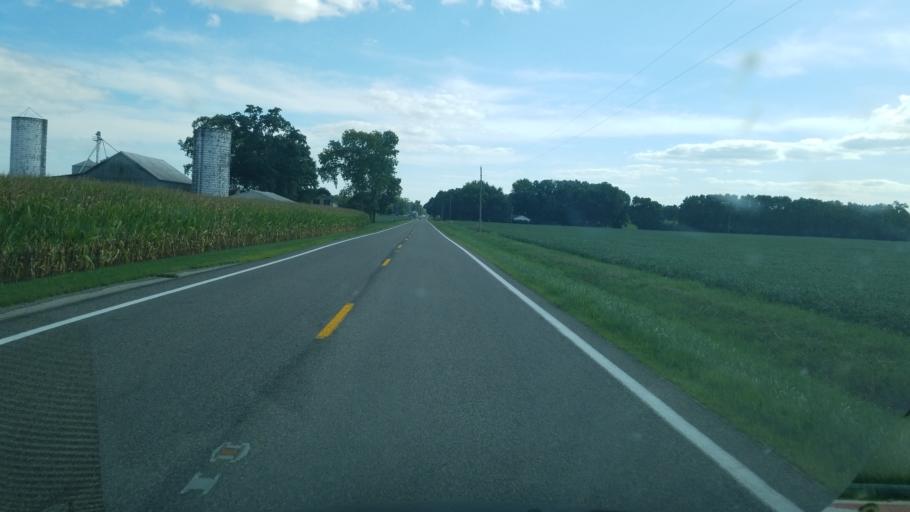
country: US
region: Ohio
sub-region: Champaign County
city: Urbana
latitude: 40.1169
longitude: -83.8367
